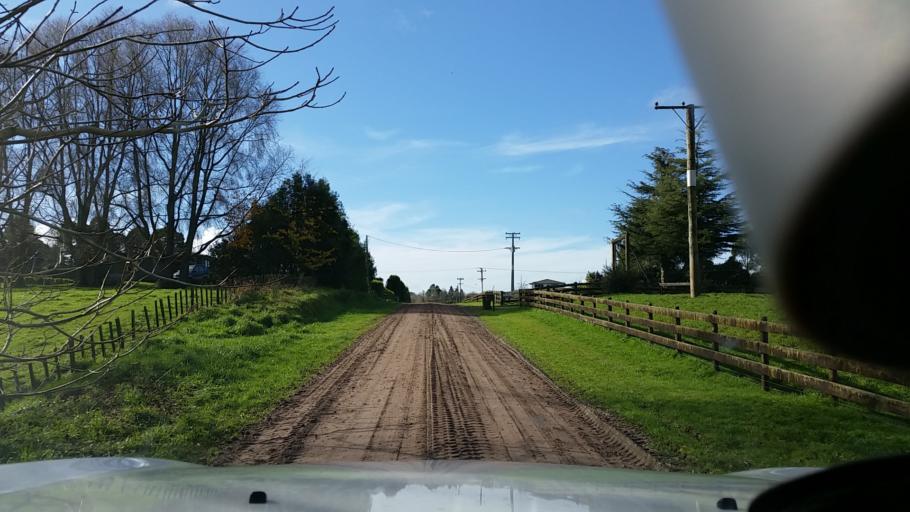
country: NZ
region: Bay of Plenty
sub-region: Rotorua District
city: Rotorua
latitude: -38.0363
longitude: 176.1967
